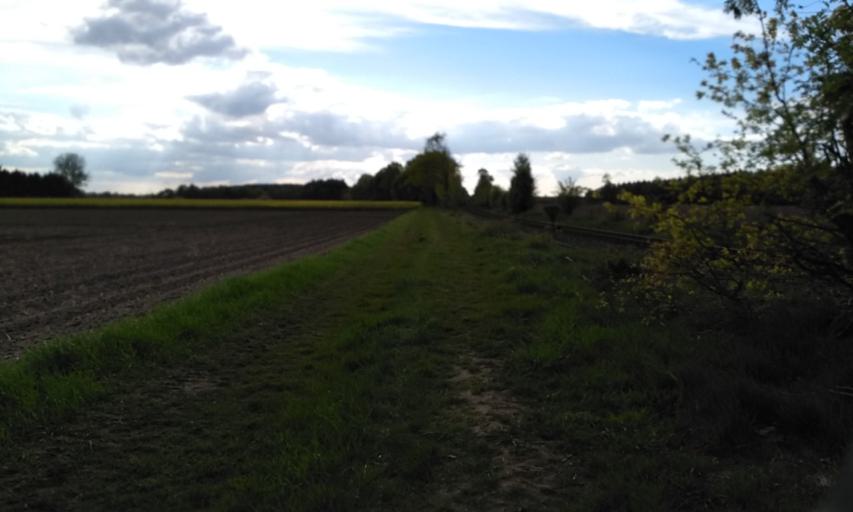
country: DE
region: Lower Saxony
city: Apensen
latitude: 53.4405
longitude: 9.6027
